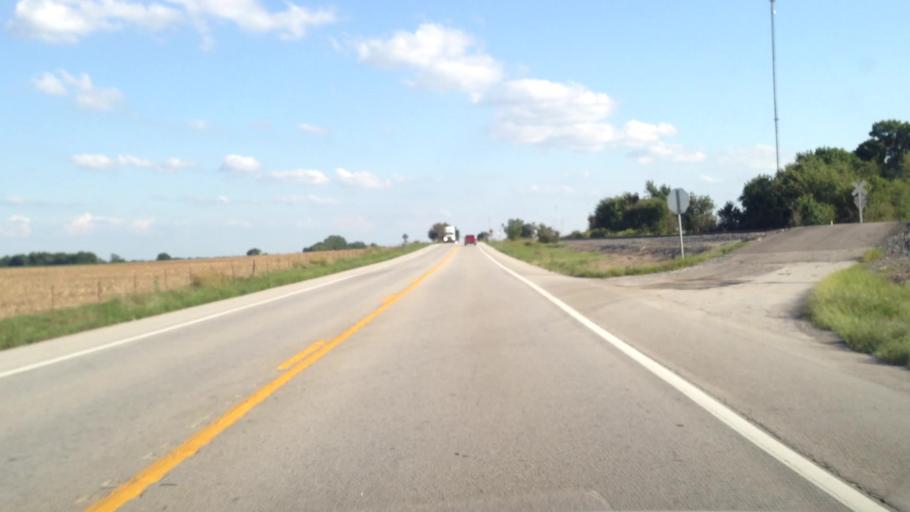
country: US
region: Missouri
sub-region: Jasper County
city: Carl Junction
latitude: 37.2644
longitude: -94.5954
